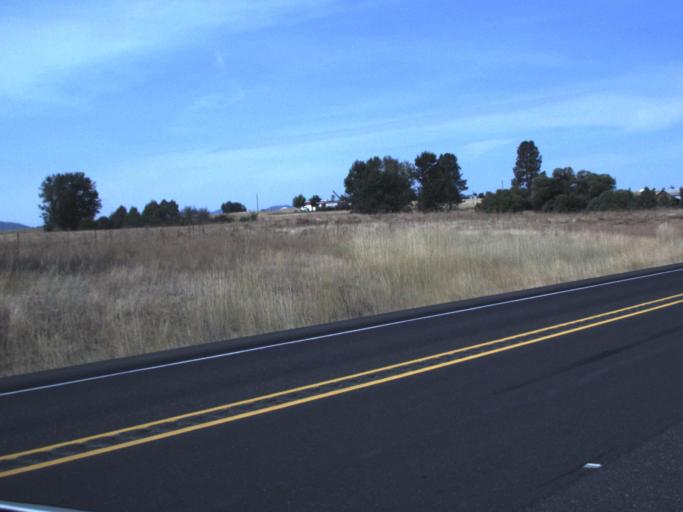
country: US
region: Washington
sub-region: Spokane County
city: Deer Park
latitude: 47.9011
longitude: -117.4373
